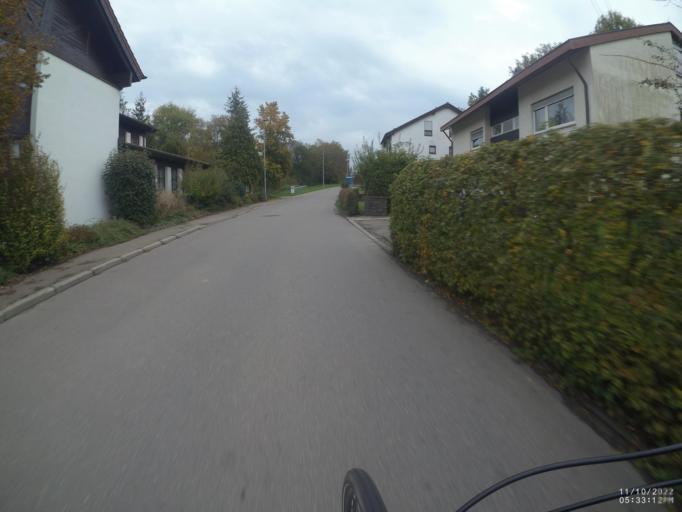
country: DE
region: Baden-Wuerttemberg
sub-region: Regierungsbezirk Stuttgart
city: Albershausen
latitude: 48.6900
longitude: 9.5702
